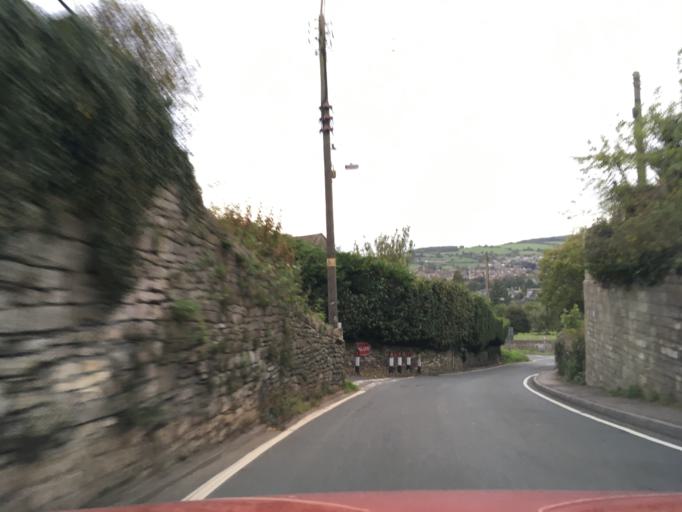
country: GB
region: England
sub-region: Gloucestershire
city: Stroud
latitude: 51.7346
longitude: -2.2409
